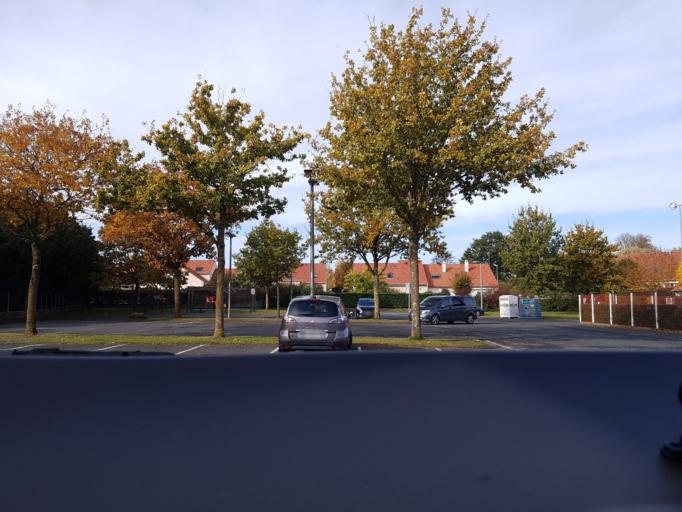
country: FR
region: Pays de la Loire
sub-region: Departement de Maine-et-Loire
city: Cholet
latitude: 47.0676
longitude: -0.8982
